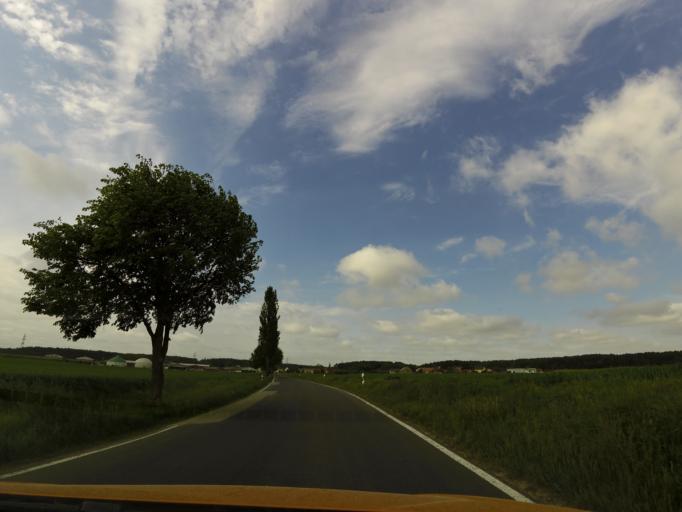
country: DE
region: Brandenburg
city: Belzig
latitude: 52.1010
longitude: 12.6268
